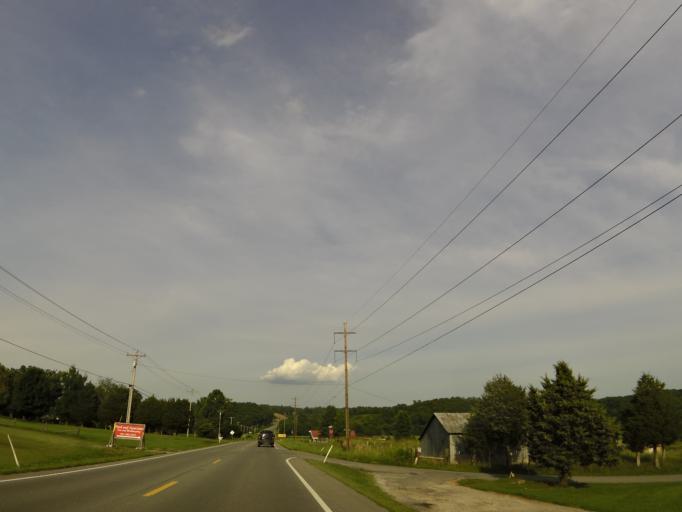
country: US
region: Tennessee
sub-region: Humphreys County
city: McEwen
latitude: 36.0974
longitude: -87.5938
